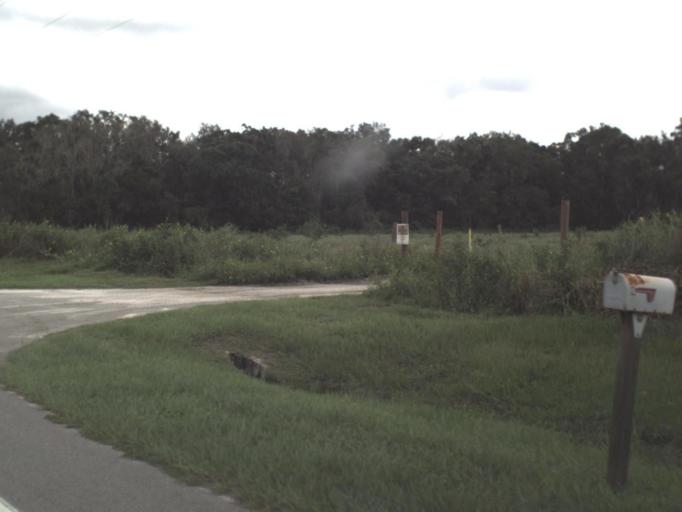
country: US
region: Florida
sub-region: Hillsborough County
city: Wimauma
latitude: 27.5807
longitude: -82.1899
